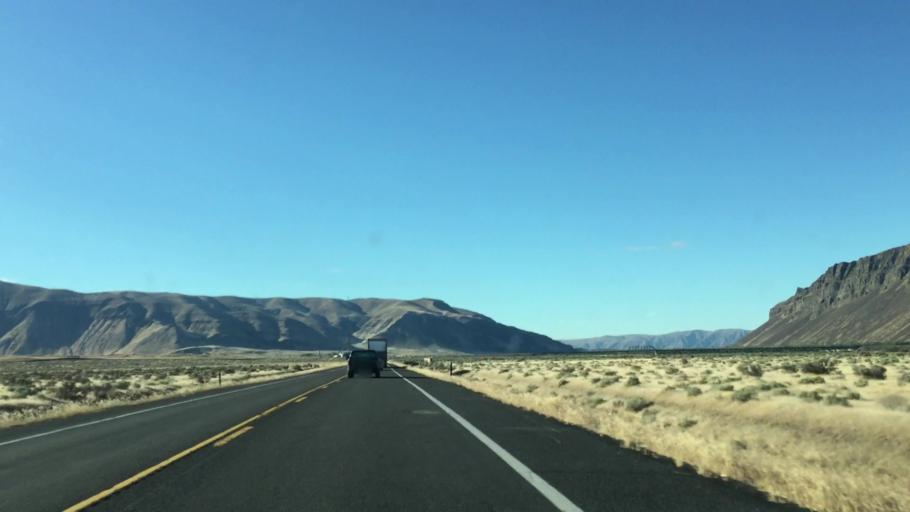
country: US
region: Washington
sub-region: Grant County
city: Mattawa
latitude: 46.8569
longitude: -119.9473
